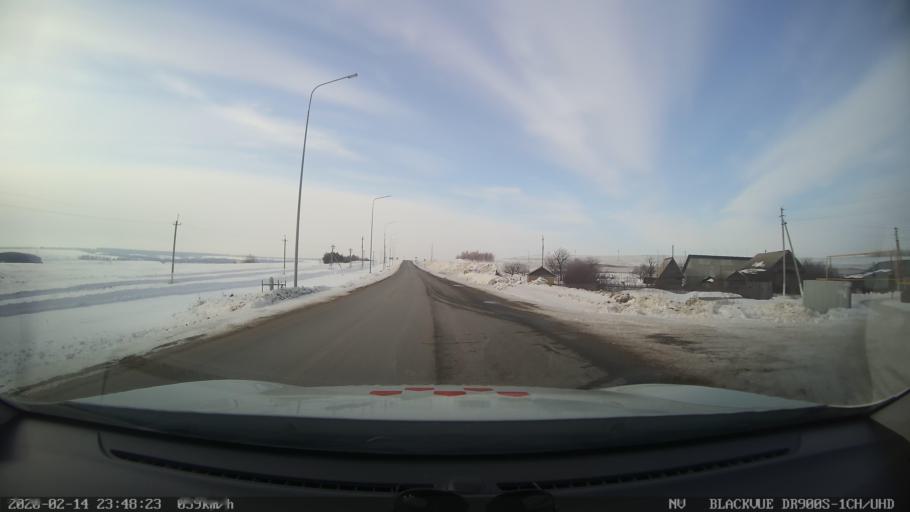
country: RU
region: Tatarstan
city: Kuybyshevskiy Zaton
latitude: 55.2476
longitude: 49.2032
